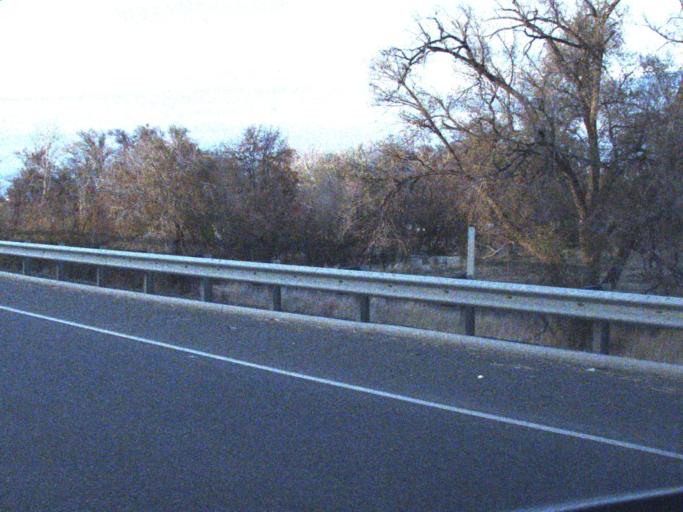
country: US
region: Washington
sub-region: Walla Walla County
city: Burbank
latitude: 46.2115
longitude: -119.0161
